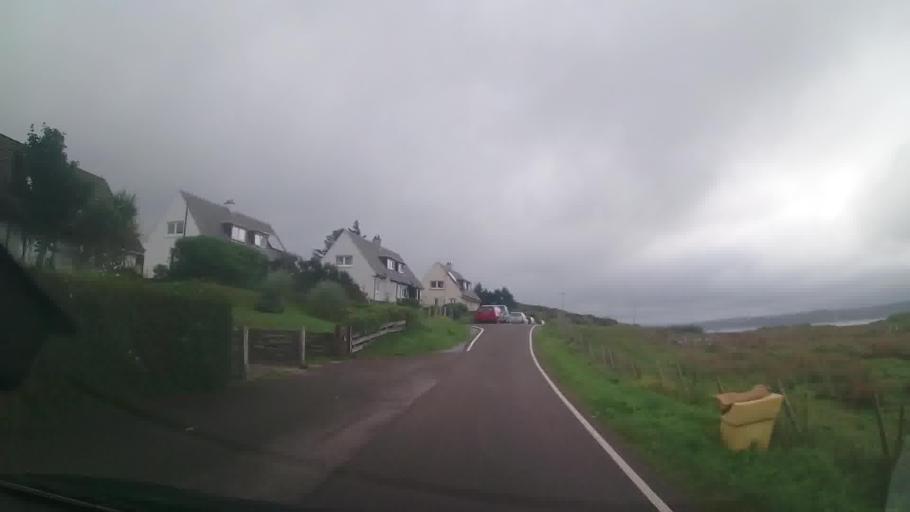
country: GB
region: Scotland
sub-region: Argyll and Bute
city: Isle Of Mull
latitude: 56.6937
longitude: -6.0960
